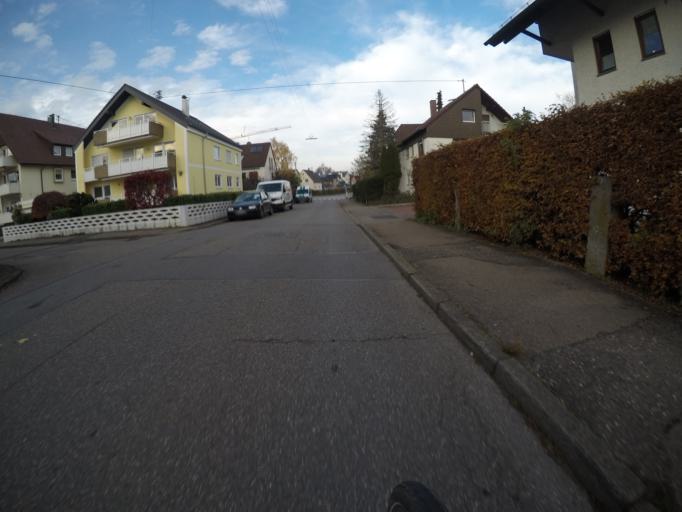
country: DE
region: Baden-Wuerttemberg
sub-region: Regierungsbezirk Stuttgart
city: Leinfelden-Echterdingen
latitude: 48.6862
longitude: 9.1633
